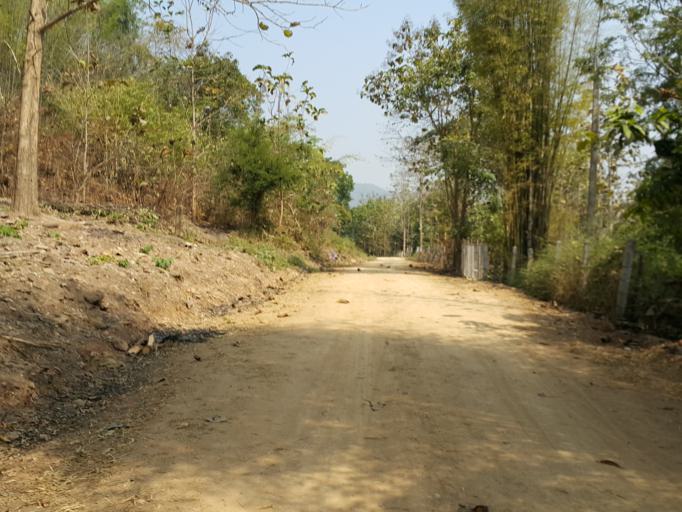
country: TH
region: Sukhothai
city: Thung Saliam
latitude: 17.3323
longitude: 99.4593
